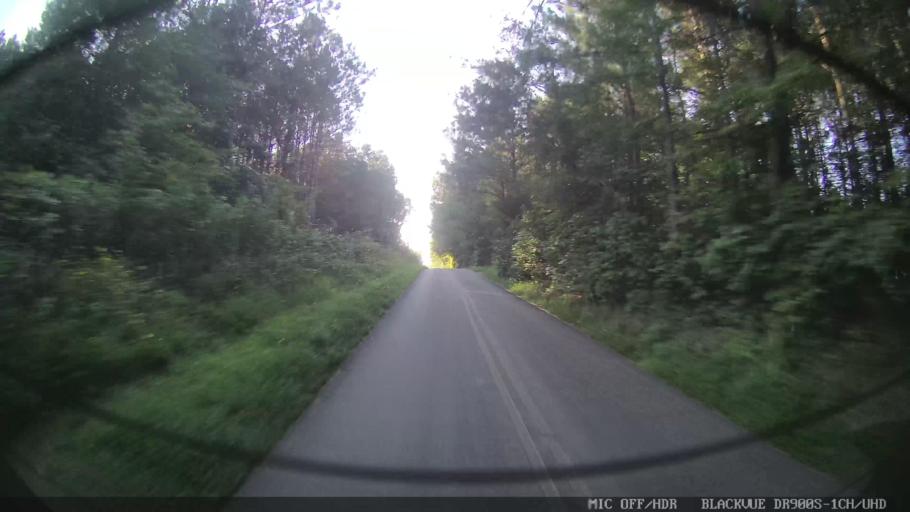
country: US
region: Tennessee
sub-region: Bradley County
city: Wildwood Lake
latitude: 35.0207
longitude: -84.7649
